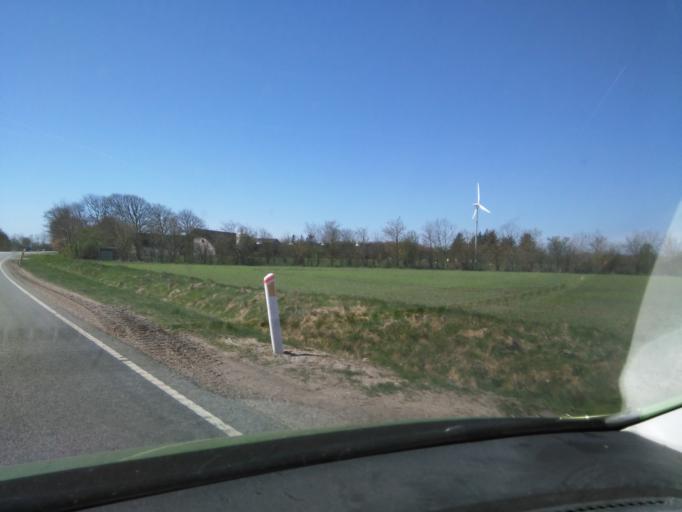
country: DK
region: South Denmark
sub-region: Varde Kommune
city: Varde
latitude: 55.6561
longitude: 8.5560
